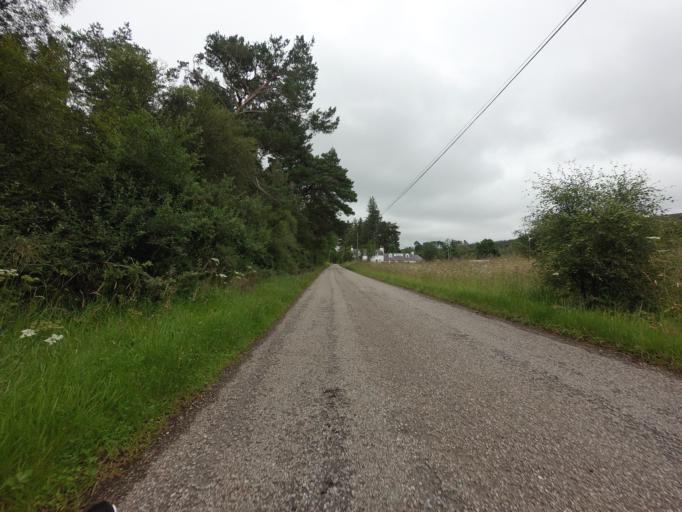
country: GB
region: Scotland
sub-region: Highland
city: Alness
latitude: 57.9912
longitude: -4.4111
